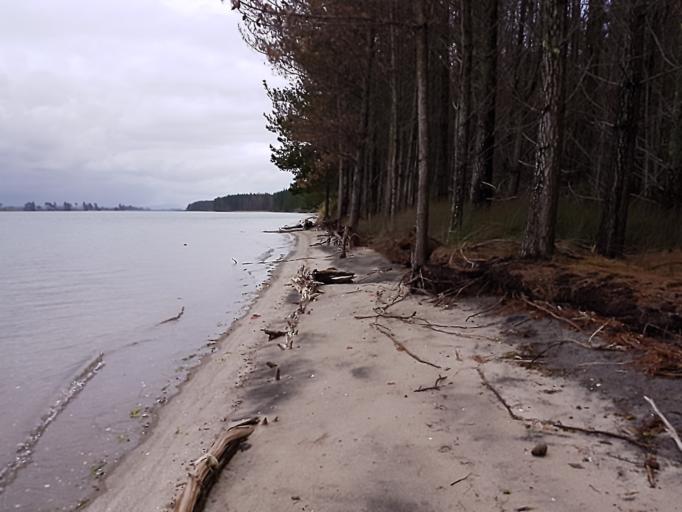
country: NZ
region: Bay of Plenty
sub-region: Tauranga City
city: Tauranga
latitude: -37.6388
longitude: 176.1428
